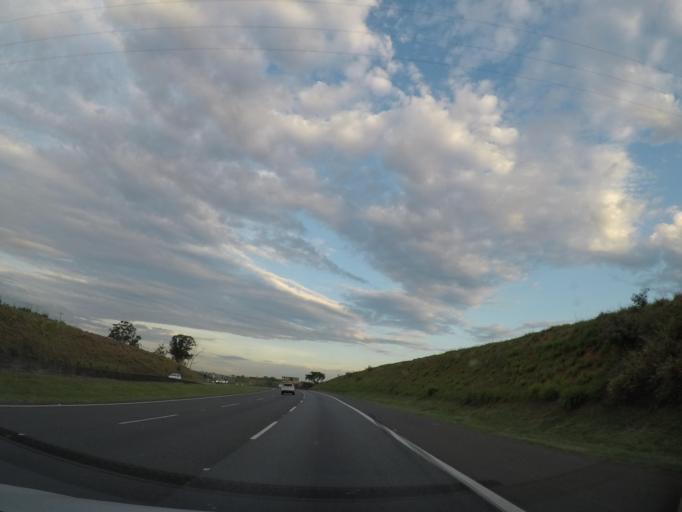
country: BR
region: Sao Paulo
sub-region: Campinas
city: Campinas
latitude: -22.9212
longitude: -47.1462
